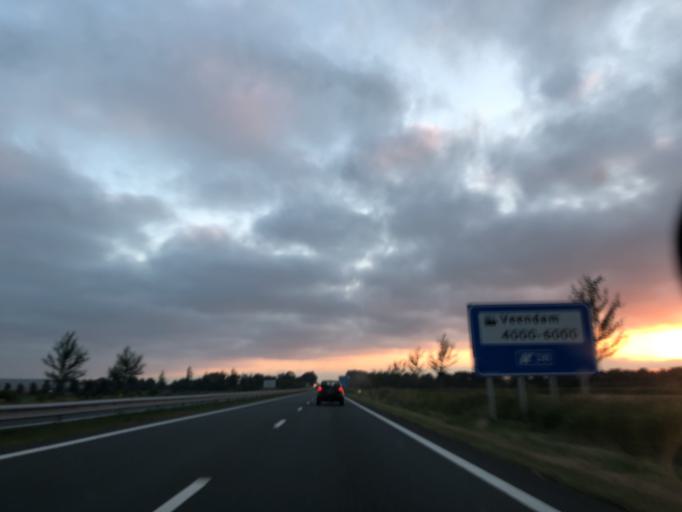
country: NL
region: Groningen
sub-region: Gemeente Veendam
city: Veendam
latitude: 53.0861
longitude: 6.8876
